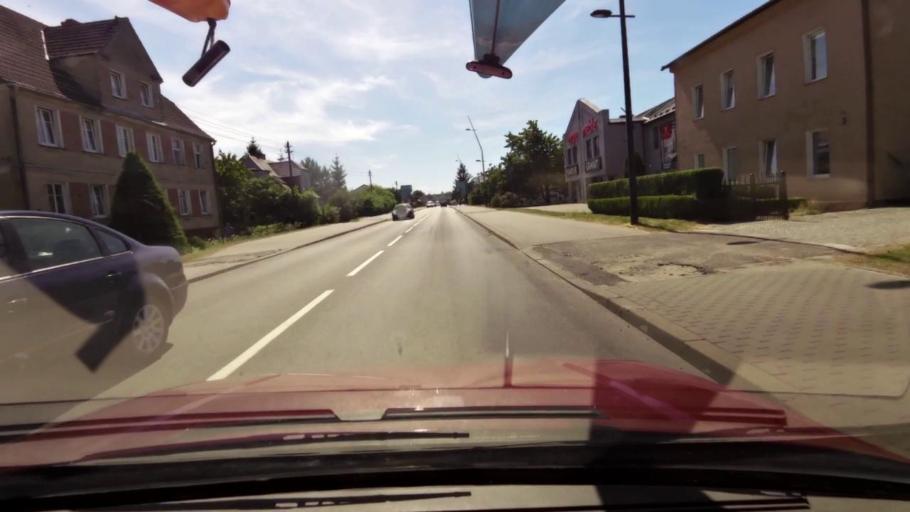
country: PL
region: Pomeranian Voivodeship
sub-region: Powiat slupski
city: Kobylnica
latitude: 54.4454
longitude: 17.0047
